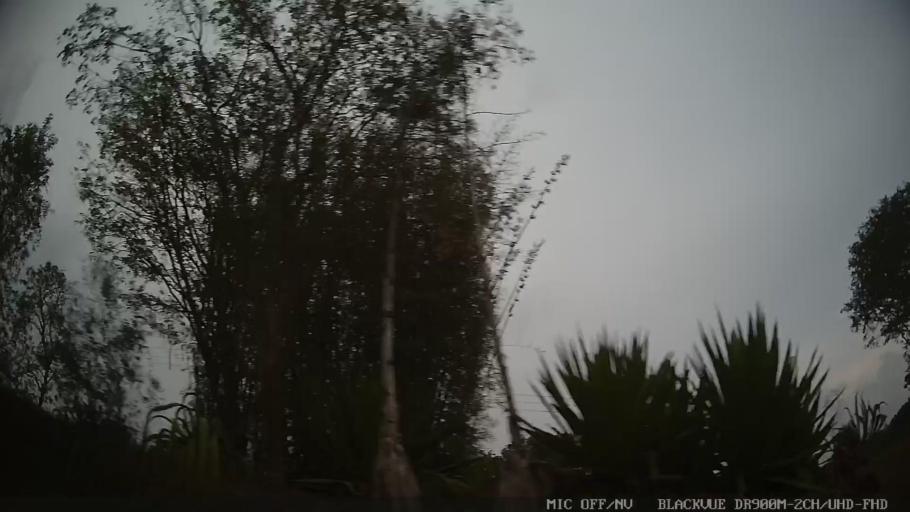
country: BR
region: Sao Paulo
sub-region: Braganca Paulista
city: Braganca Paulista
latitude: -22.9453
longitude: -46.6413
